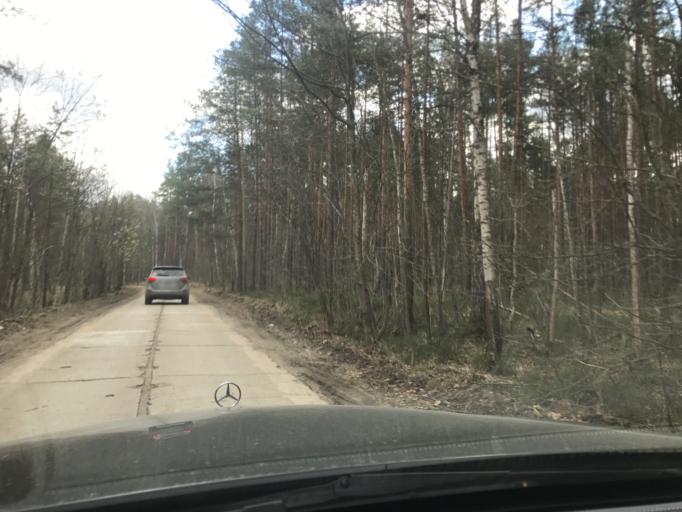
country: RU
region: Moskovskaya
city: Vereya
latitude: 55.8402
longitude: 39.1286
